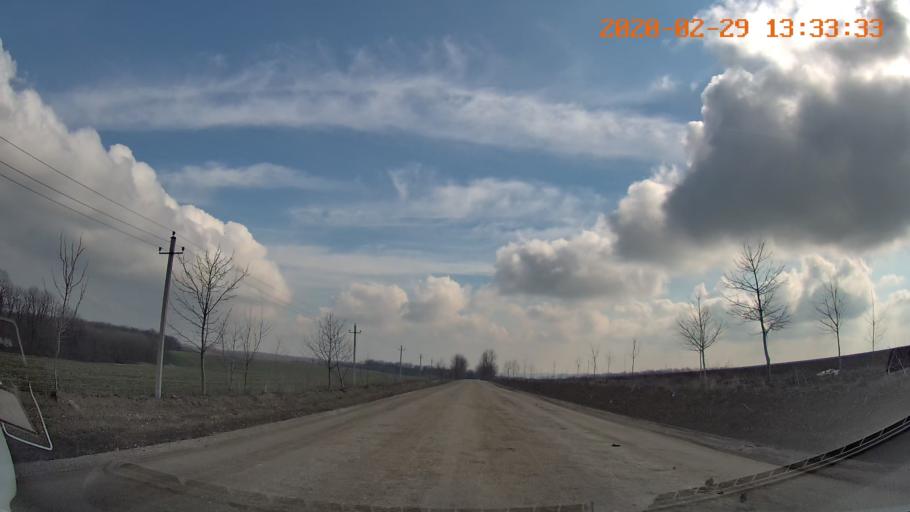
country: MD
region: Telenesti
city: Camenca
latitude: 47.8730
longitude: 28.6173
